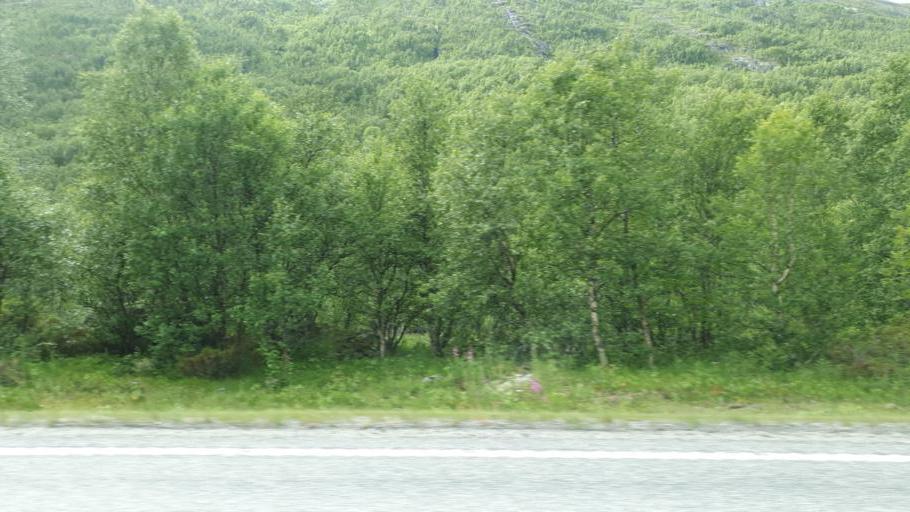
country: NO
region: Sor-Trondelag
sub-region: Oppdal
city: Oppdal
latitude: 62.4026
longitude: 9.6364
